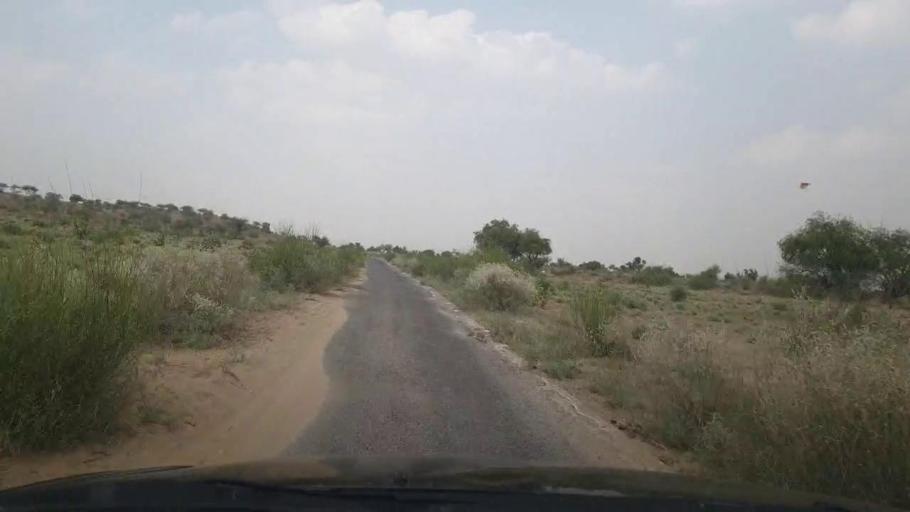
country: PK
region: Sindh
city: Islamkot
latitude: 24.9171
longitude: 70.5627
